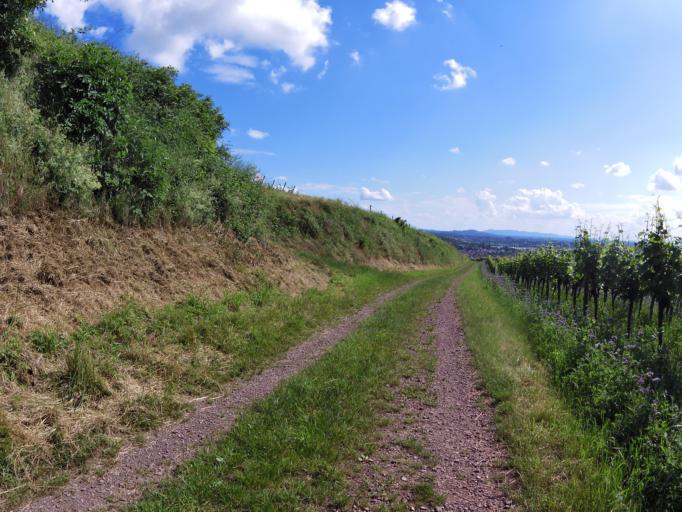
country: DE
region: Baden-Wuerttemberg
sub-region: Freiburg Region
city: Lahr
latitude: 48.3471
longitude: 7.8517
